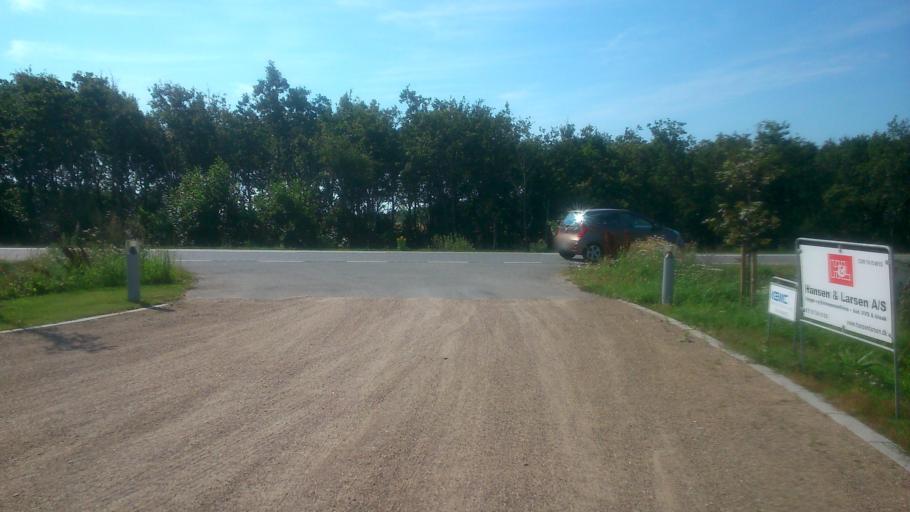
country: DK
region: Central Jutland
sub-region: Ringkobing-Skjern Kommune
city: Skjern
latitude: 56.0834
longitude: 8.4228
